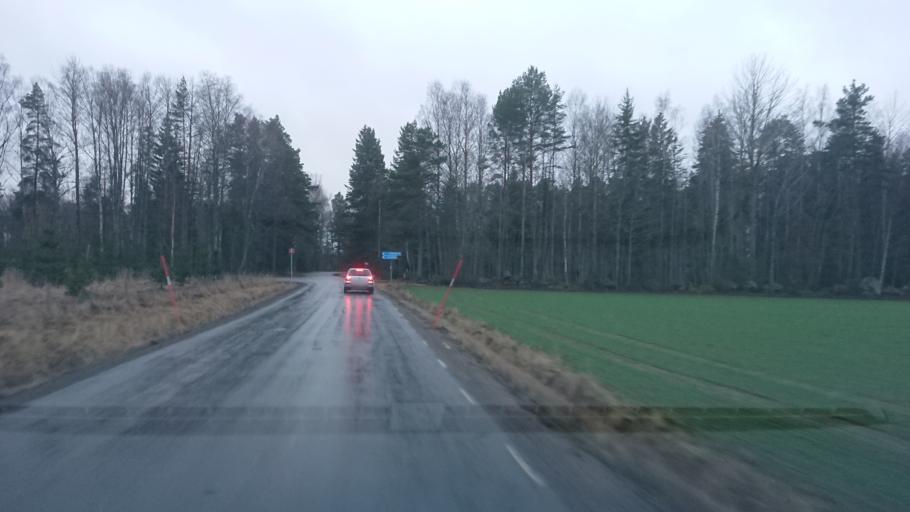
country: SE
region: Uppsala
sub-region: Osthammars Kommun
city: Bjorklinge
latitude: 59.9799
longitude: 17.5954
